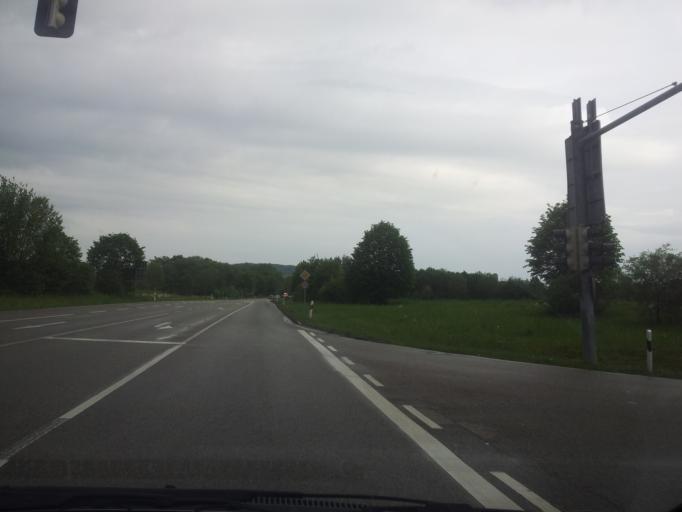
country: DE
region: Baden-Wuerttemberg
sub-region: Regierungsbezirk Stuttgart
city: Abstatt
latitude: 49.0576
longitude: 9.2715
